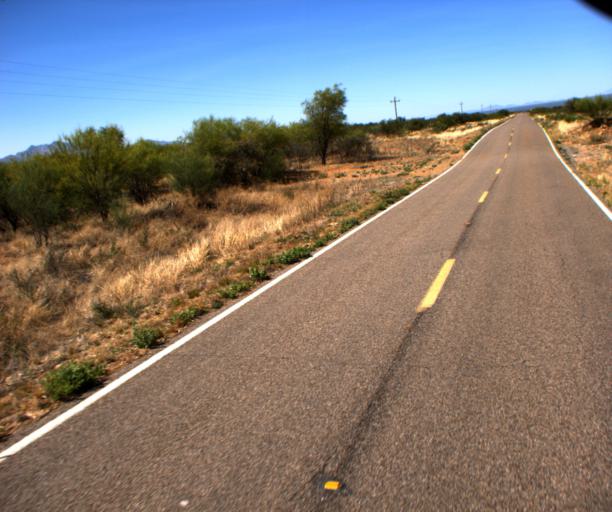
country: US
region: Arizona
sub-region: Pima County
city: Three Points
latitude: 31.7592
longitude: -111.4759
